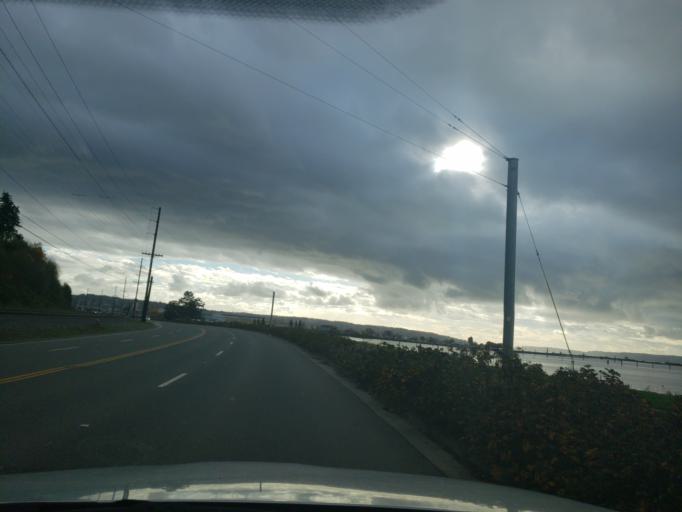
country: US
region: Washington
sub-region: Snohomish County
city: Everett
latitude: 48.0095
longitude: -122.2136
